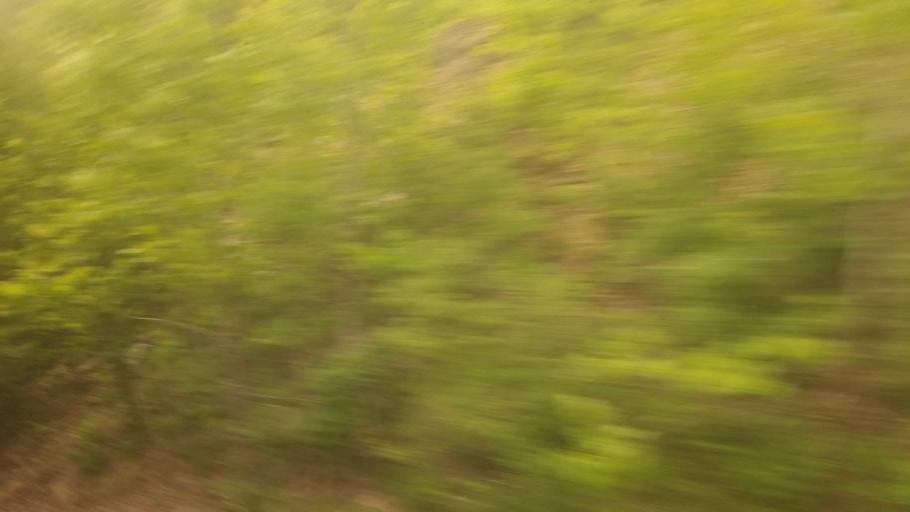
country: US
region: Kansas
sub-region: Shawnee County
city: Topeka
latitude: 39.0527
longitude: -95.4960
